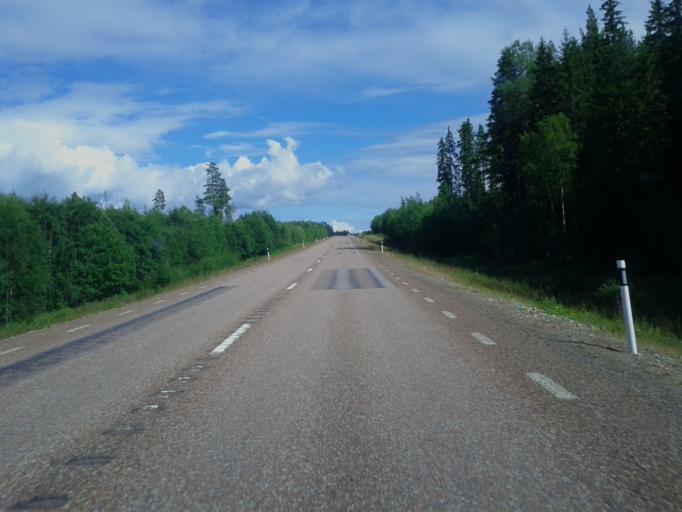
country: SE
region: Dalarna
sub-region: Rattviks Kommun
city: Raettvik
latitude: 60.8410
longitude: 15.2034
